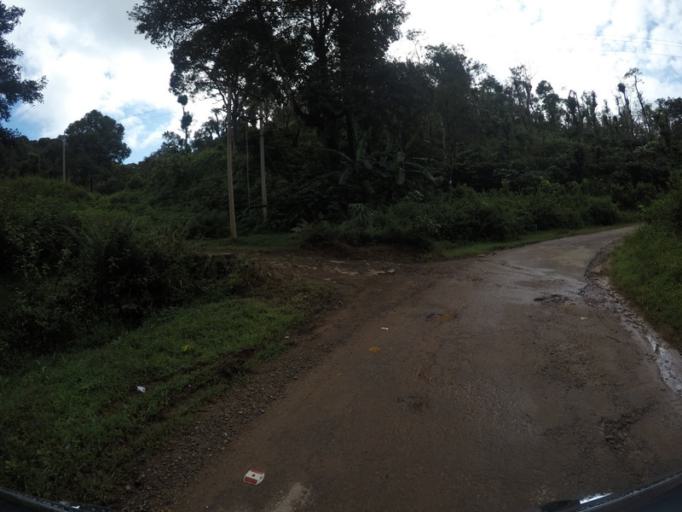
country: IN
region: Karnataka
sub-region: Kodagu
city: Madikeri
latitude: 12.4610
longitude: 75.7671
